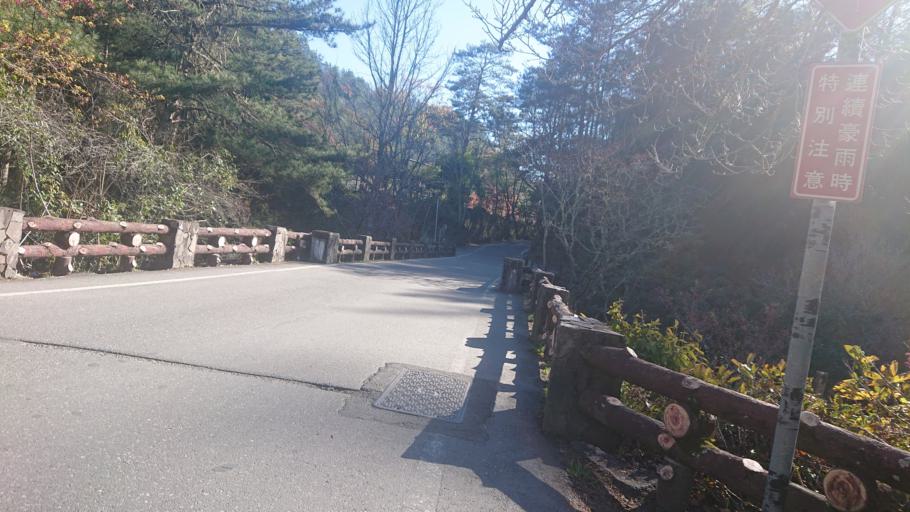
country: TW
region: Taiwan
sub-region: Hualien
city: Hualian
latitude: 24.3564
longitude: 121.3123
